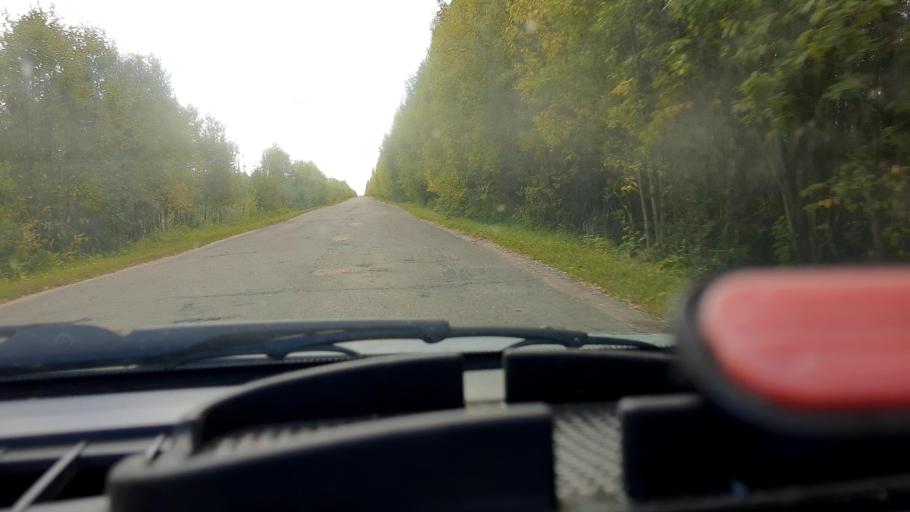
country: RU
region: Mariy-El
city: Kilemary
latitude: 56.9044
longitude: 46.7378
